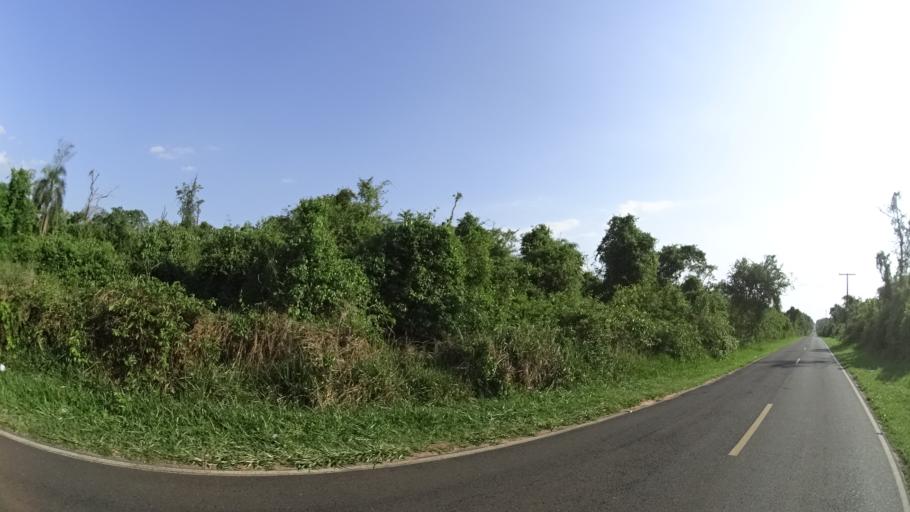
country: BR
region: Sao Paulo
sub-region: Urupes
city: Urupes
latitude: -21.3767
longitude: -49.4813
